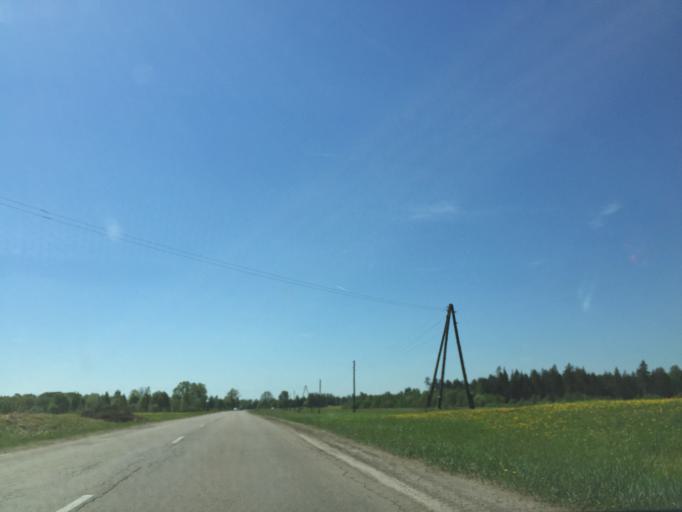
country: LV
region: Malpils
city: Malpils
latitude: 56.9226
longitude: 24.9370
